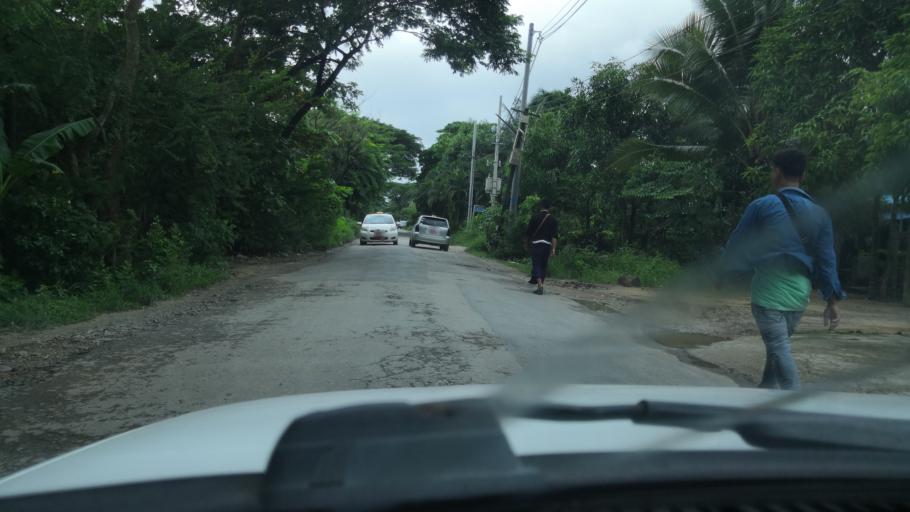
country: MM
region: Yangon
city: Yangon
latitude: 16.8801
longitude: 96.1801
